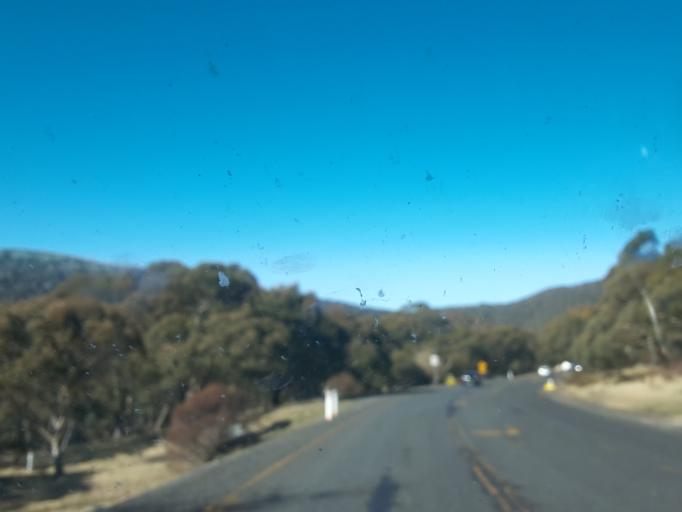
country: AU
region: New South Wales
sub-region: Snowy River
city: Jindabyne
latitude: -36.4495
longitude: 148.4515
